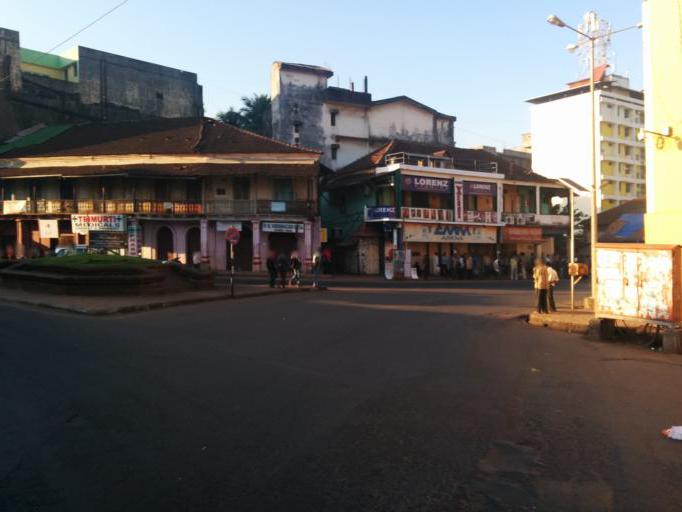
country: IN
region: Goa
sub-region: South Goa
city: Madgaon
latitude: 15.2721
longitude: 73.9587
